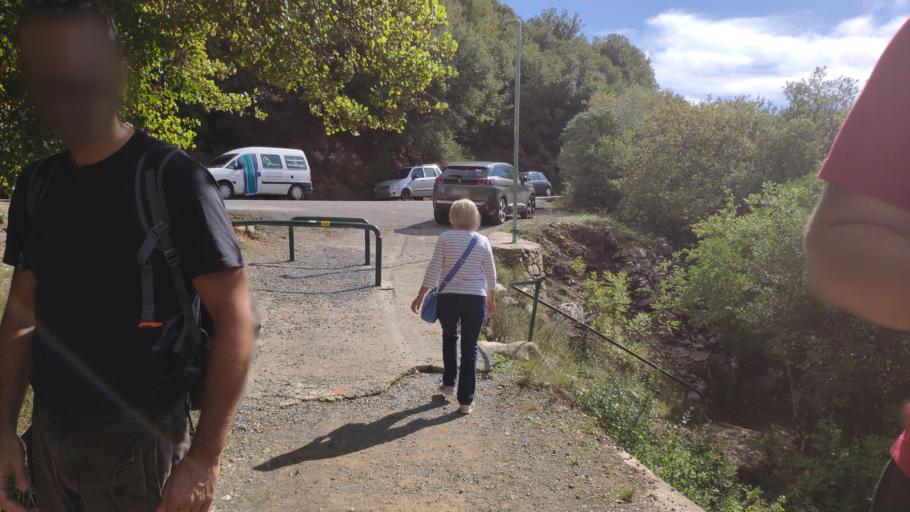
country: GR
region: Peloponnese
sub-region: Nomos Arkadias
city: Dimitsana
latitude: 37.5396
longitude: 22.0462
